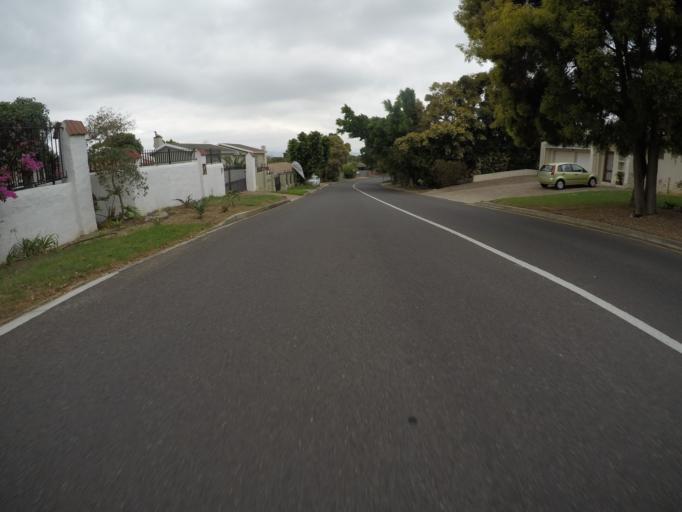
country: ZA
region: Western Cape
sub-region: City of Cape Town
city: Kraaifontein
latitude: -33.8663
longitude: 18.6486
